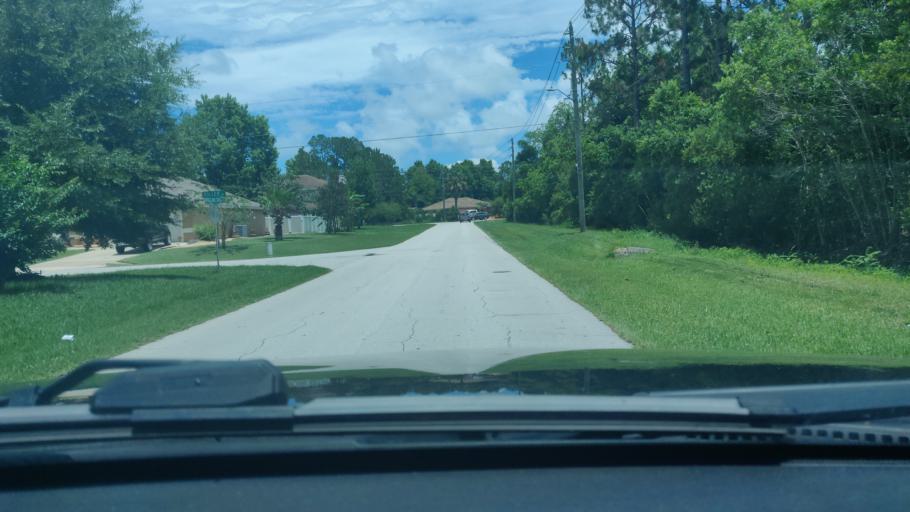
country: US
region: Florida
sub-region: Flagler County
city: Bunnell
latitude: 29.5179
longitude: -81.2575
